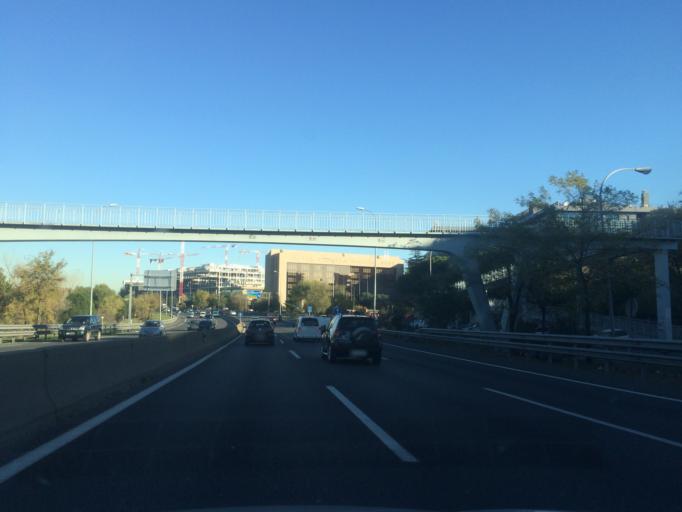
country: ES
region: Madrid
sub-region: Provincia de Madrid
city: Ciudad Lineal
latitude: 40.4489
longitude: -3.6400
